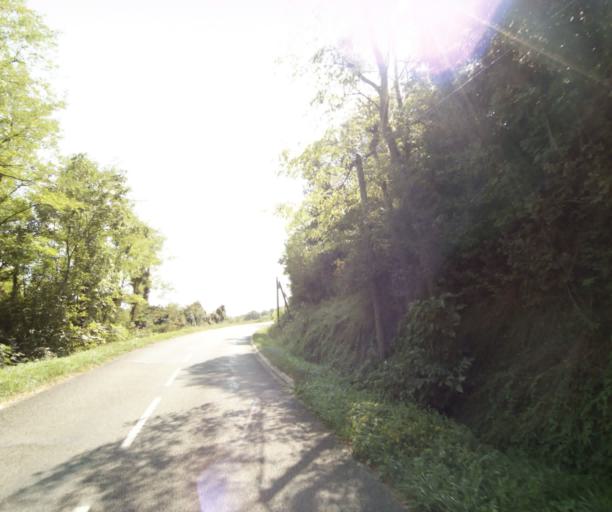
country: FR
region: Bourgogne
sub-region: Departement de Saone-et-Loire
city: Tournus
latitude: 46.5650
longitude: 4.8810
